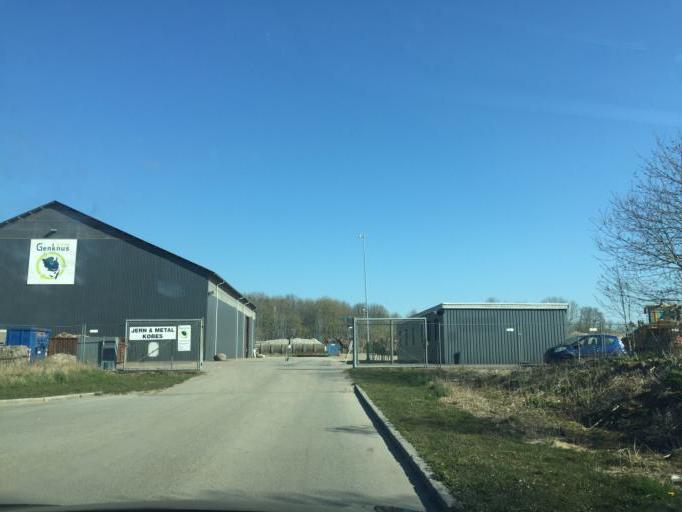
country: DK
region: South Denmark
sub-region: Faaborg-Midtfyn Kommune
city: Ringe
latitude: 55.2515
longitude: 10.4885
